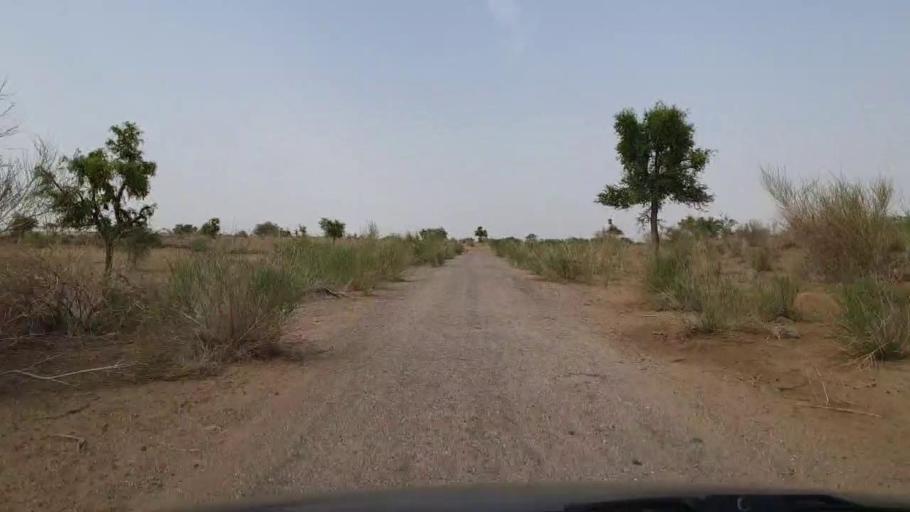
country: PK
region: Sindh
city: Chor
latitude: 25.4736
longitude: 70.5229
